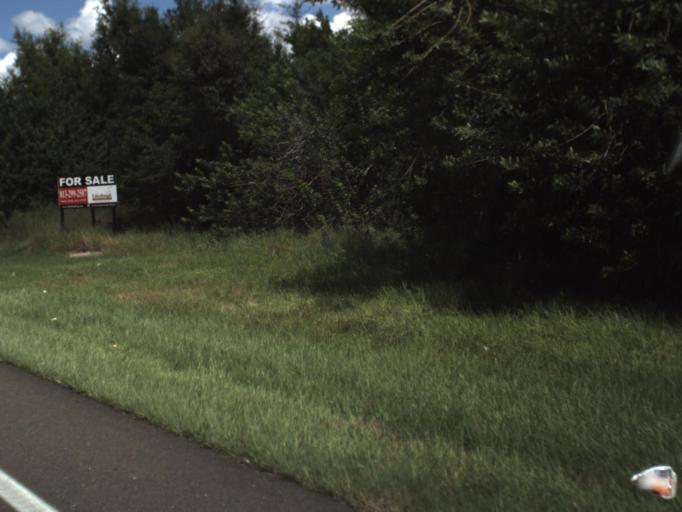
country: US
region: Florida
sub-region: Polk County
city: Winter Haven
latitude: 28.0556
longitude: -81.7217
